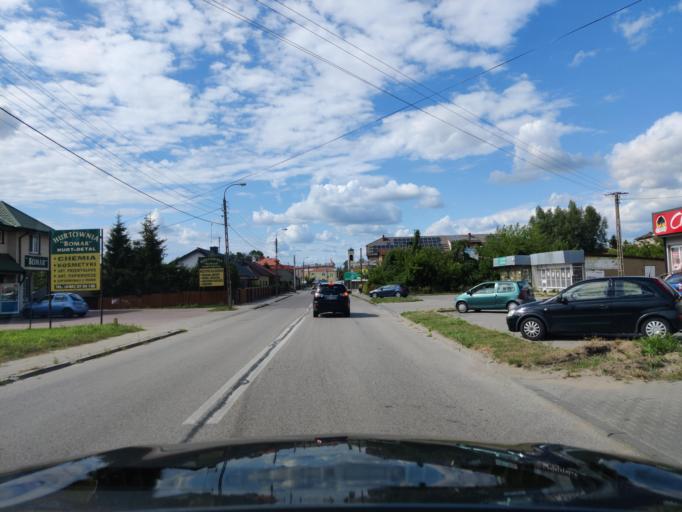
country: PL
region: Podlasie
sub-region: Powiat wysokomazowiecki
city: Czyzew
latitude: 52.7955
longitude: 22.3140
